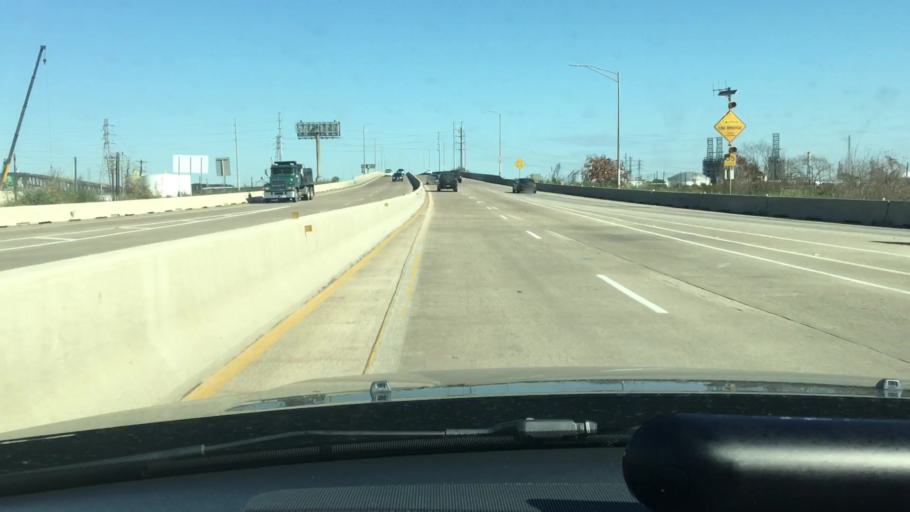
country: US
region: Texas
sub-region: Harris County
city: Deer Park
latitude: 29.7168
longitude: -95.1513
